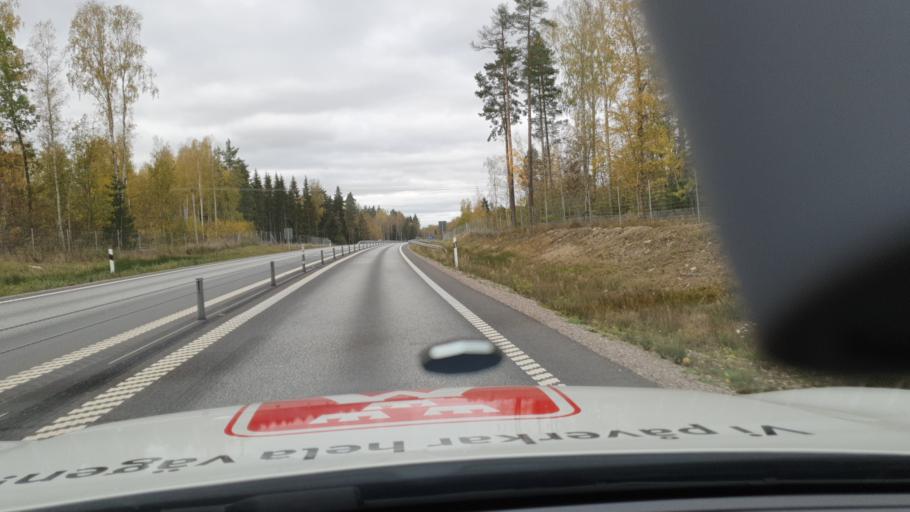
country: SE
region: OErebro
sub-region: Hallsbergs Kommun
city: Skollersta
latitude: 59.1207
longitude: 15.2930
